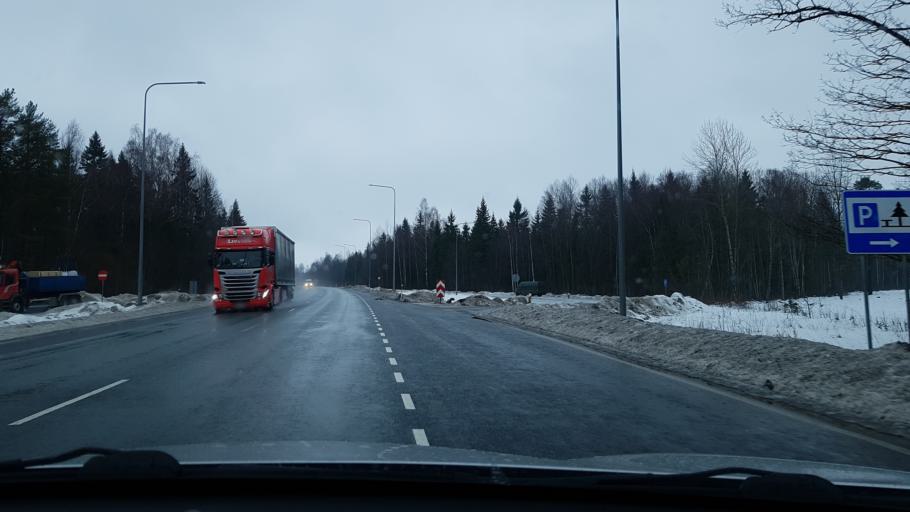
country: EE
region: Raplamaa
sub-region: Kohila vald
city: Kohila
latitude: 59.1293
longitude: 24.7912
